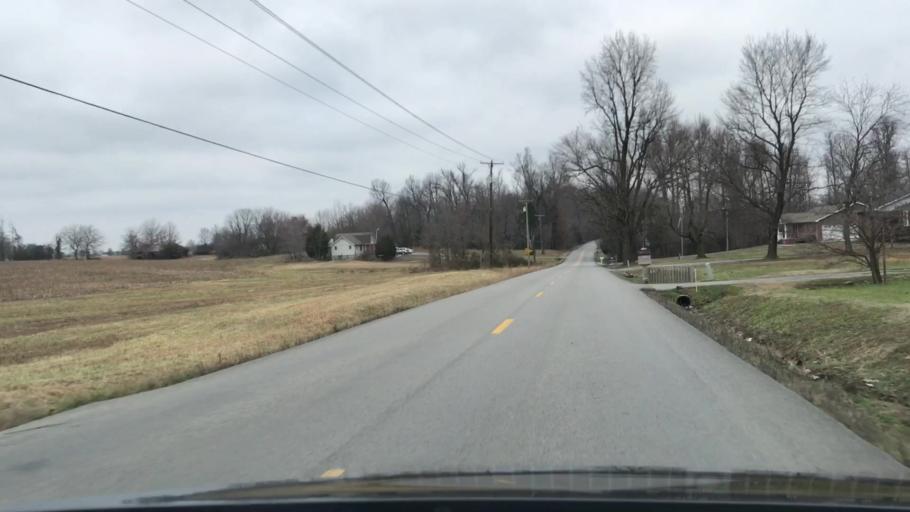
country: US
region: Kentucky
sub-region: Muhlenberg County
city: Morehead
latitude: 37.3609
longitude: -87.2330
